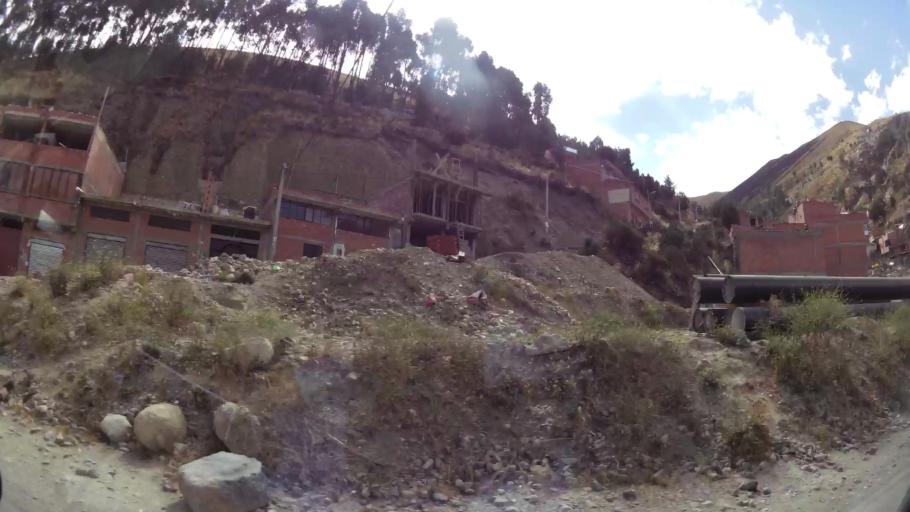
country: BO
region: La Paz
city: La Paz
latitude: -16.4622
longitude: -68.1091
